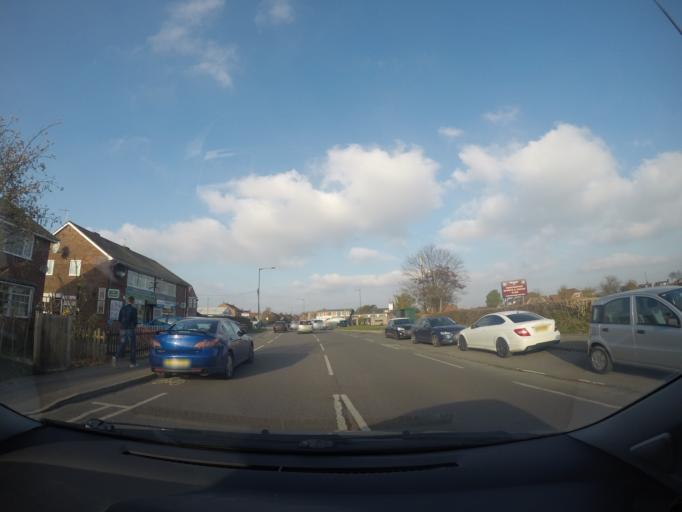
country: GB
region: England
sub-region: City of York
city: Huntington
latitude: 53.9976
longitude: -1.0574
